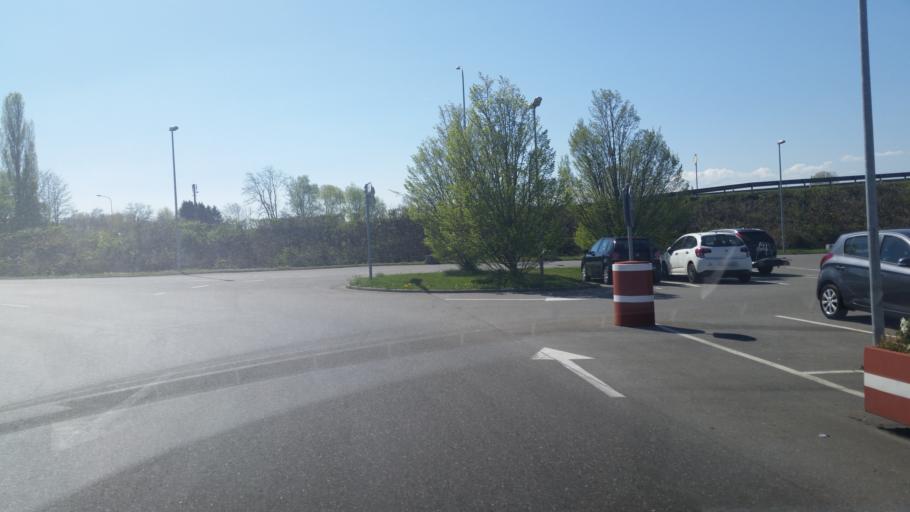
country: CH
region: Vaud
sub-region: Broye-Vully District
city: Avenches
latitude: 46.8813
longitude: 7.0439
